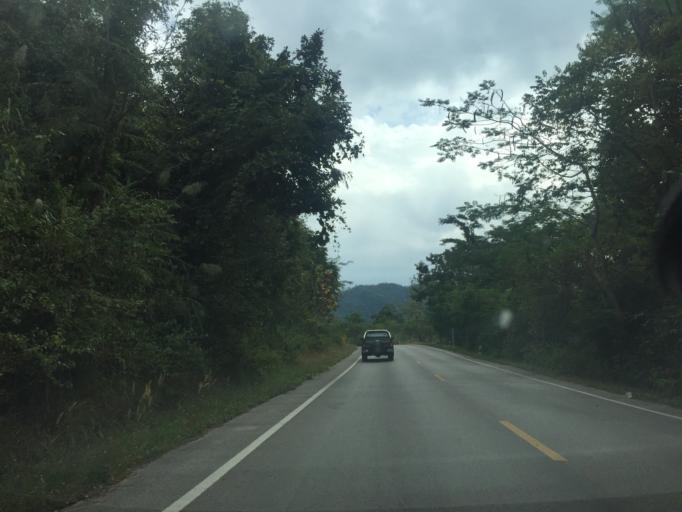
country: TH
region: Lampang
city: Mueang Pan
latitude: 18.7824
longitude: 99.5239
